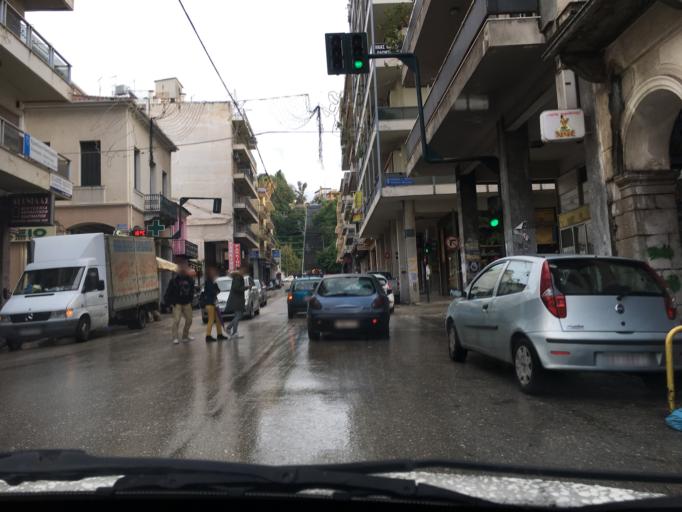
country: GR
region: West Greece
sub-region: Nomos Achaias
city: Patra
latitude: 38.2464
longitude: 21.7380
